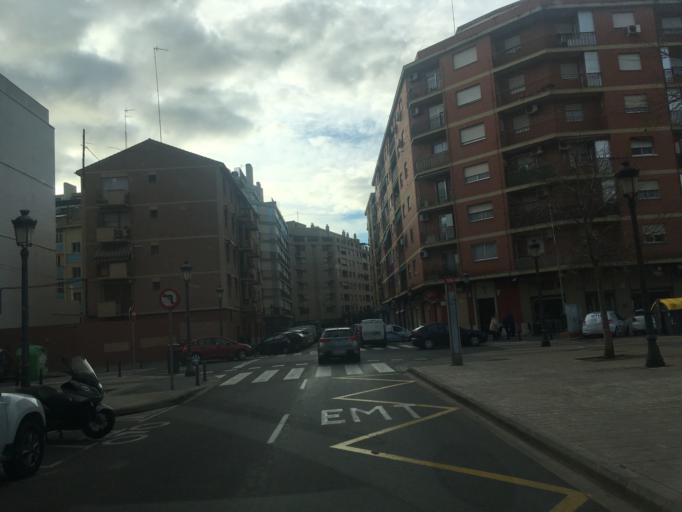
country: ES
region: Valencia
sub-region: Provincia de Valencia
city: Mislata
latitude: 39.4711
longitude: -0.4027
